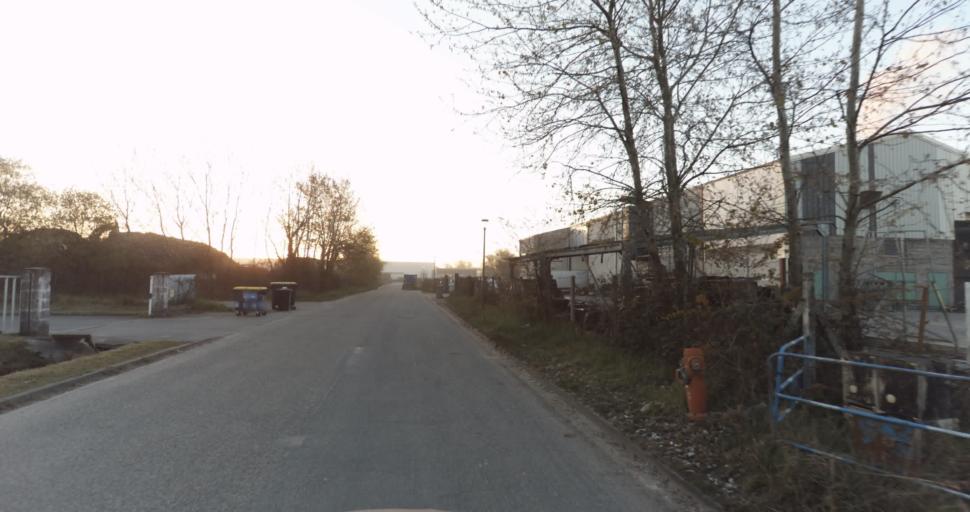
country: FR
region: Aquitaine
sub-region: Departement de la Gironde
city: Martignas-sur-Jalle
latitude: 44.8124
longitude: -0.7291
